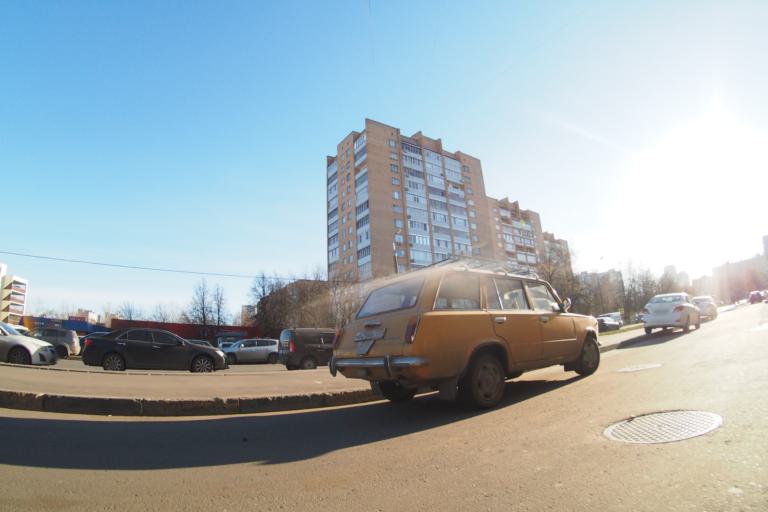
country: RU
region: Moscow
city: Zagor'ye
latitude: 55.5891
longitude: 37.6643
